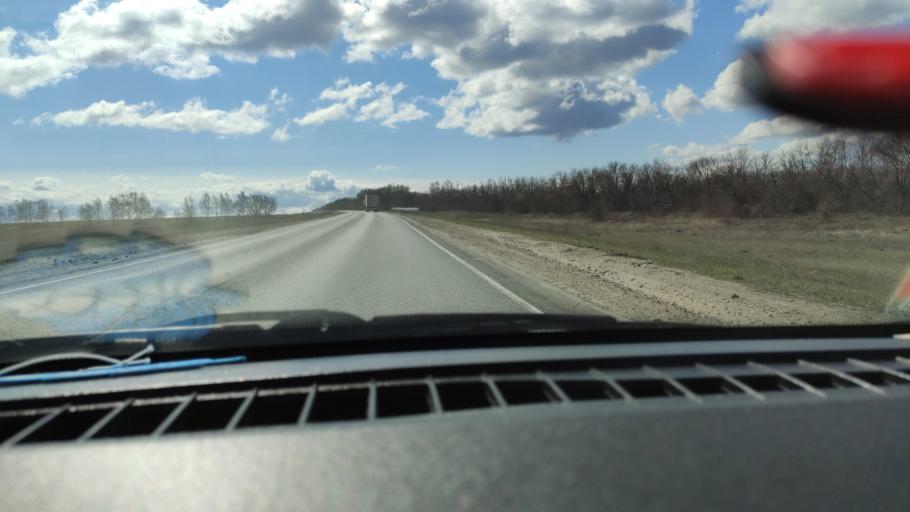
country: RU
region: Saratov
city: Dukhovnitskoye
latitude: 52.7262
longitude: 48.2605
